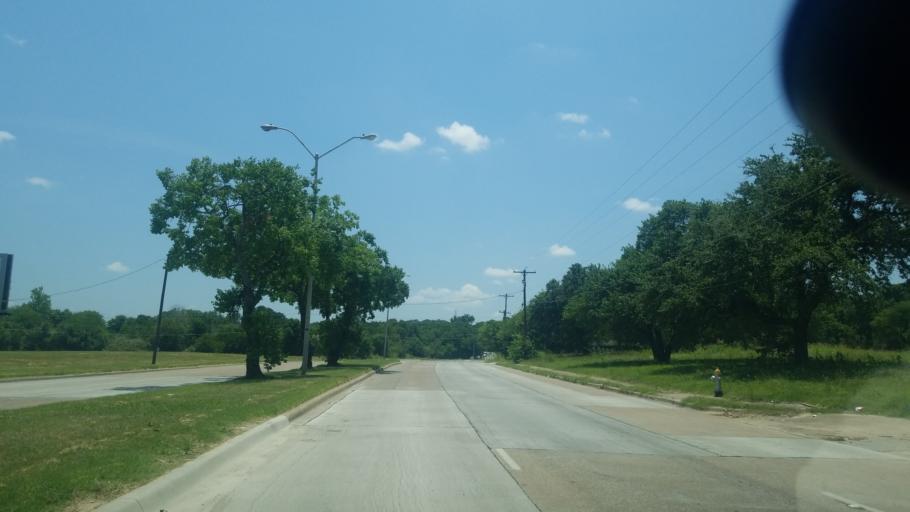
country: US
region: Texas
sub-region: Dallas County
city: Dallas
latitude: 32.7311
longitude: -96.7851
